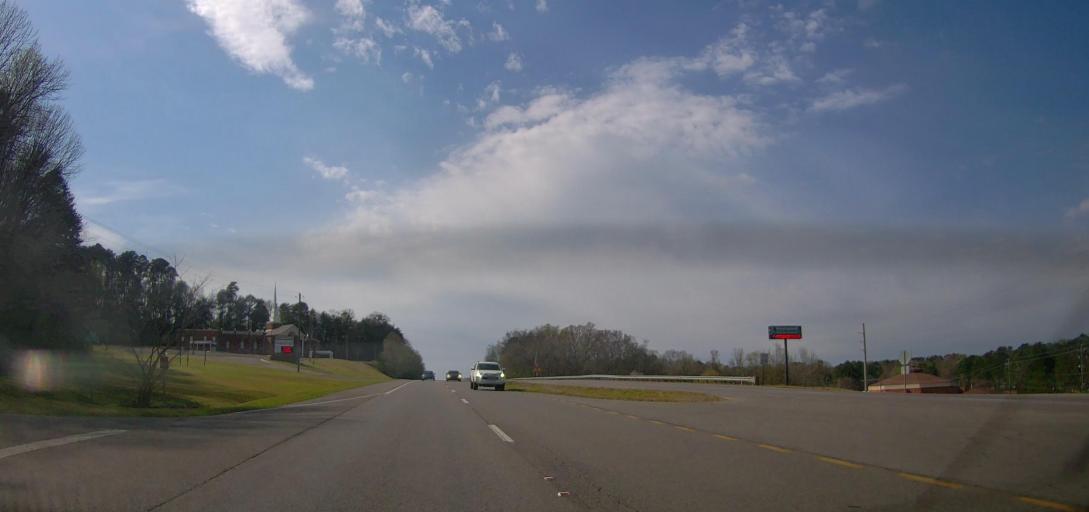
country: US
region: Alabama
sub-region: Jefferson County
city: Forestdale
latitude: 33.5781
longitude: -86.9152
